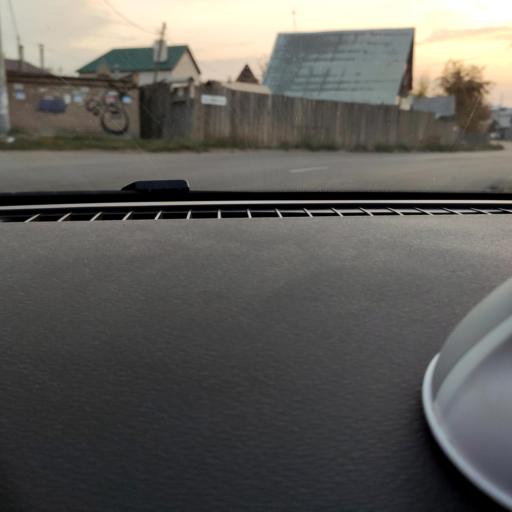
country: RU
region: Samara
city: Samara
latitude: 53.1812
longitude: 50.1075
